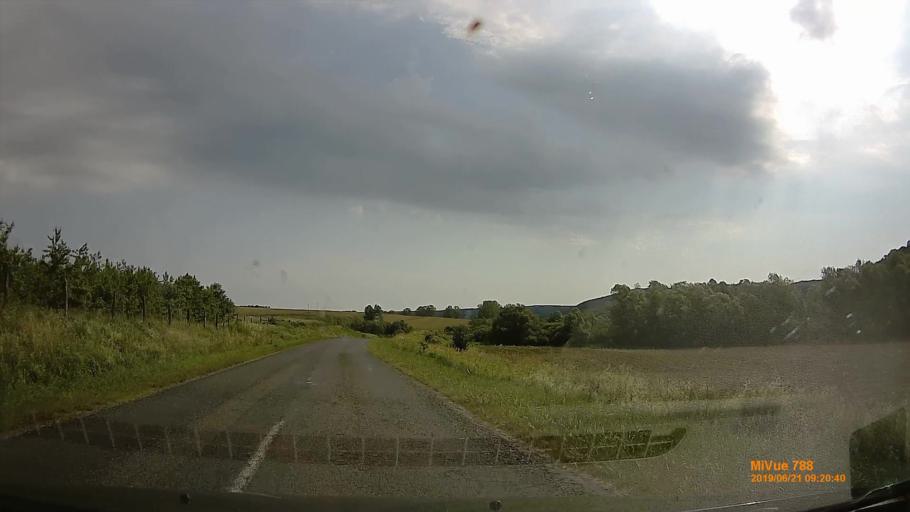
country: HU
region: Somogy
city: Taszar
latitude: 46.2364
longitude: 17.8737
